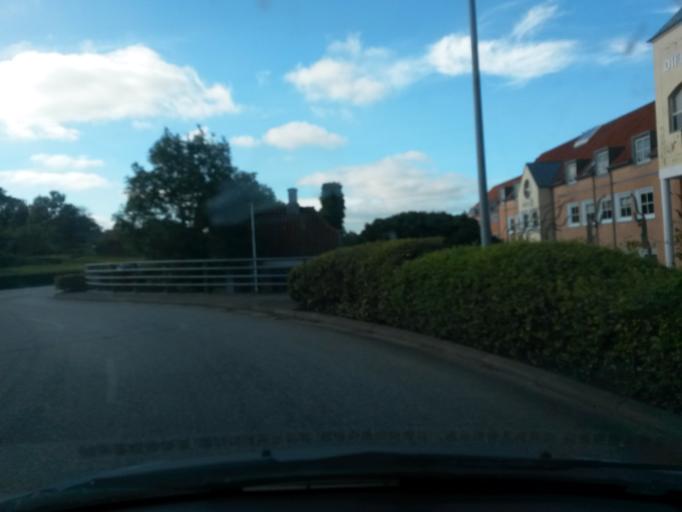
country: DK
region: Central Jutland
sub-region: Holstebro Kommune
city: Holstebro
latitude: 56.3542
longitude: 8.6185
